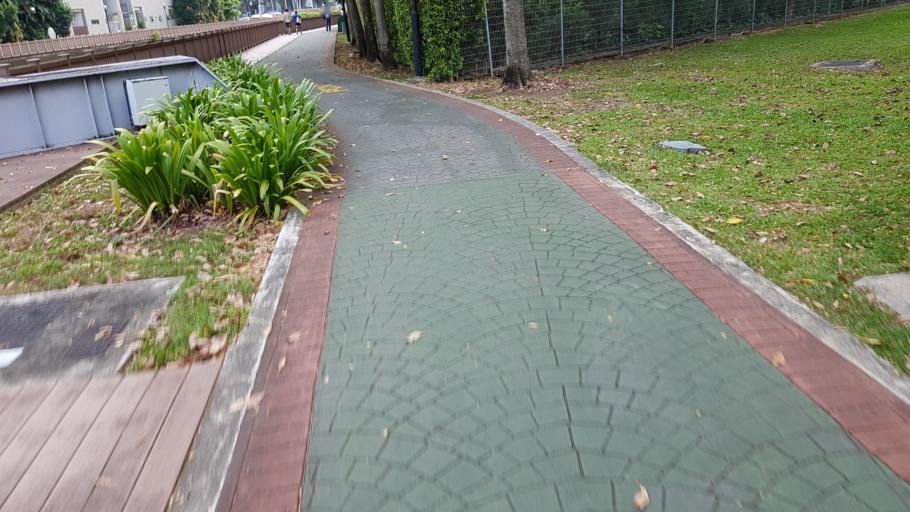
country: SG
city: Singapore
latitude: 1.2919
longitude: 103.8250
